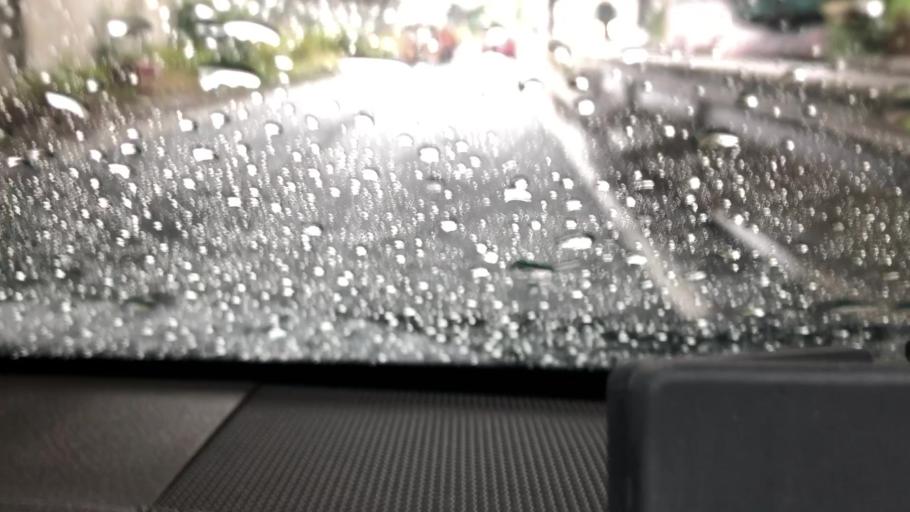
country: JP
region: Kanagawa
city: Yokohama
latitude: 35.4421
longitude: 139.5921
